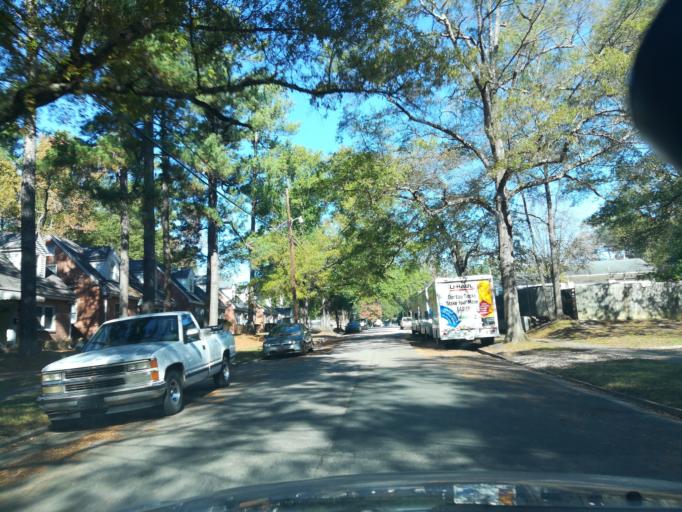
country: US
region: North Carolina
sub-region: Durham County
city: Durham
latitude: 36.0213
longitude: -78.9176
